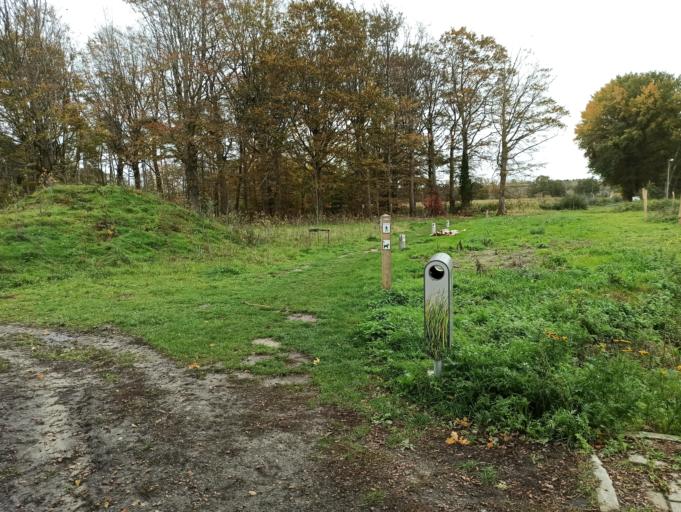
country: BE
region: Flanders
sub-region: Provincie West-Vlaanderen
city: Oostkamp
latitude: 51.1331
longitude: 3.2336
